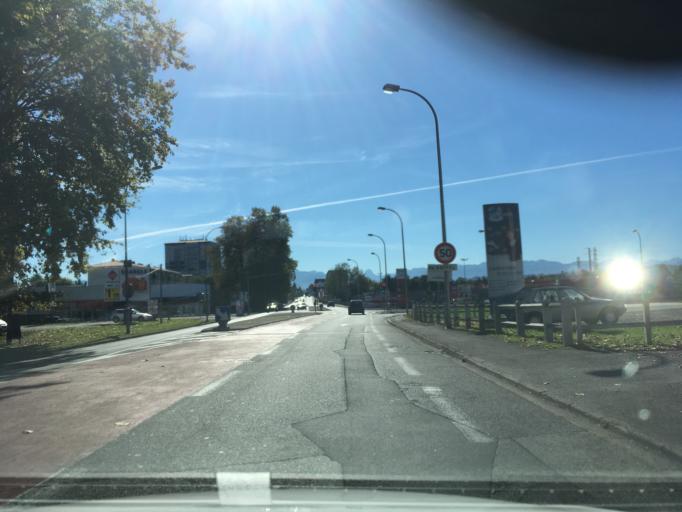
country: FR
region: Aquitaine
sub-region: Departement des Pyrenees-Atlantiques
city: Lons
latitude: 43.3302
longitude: -0.3797
